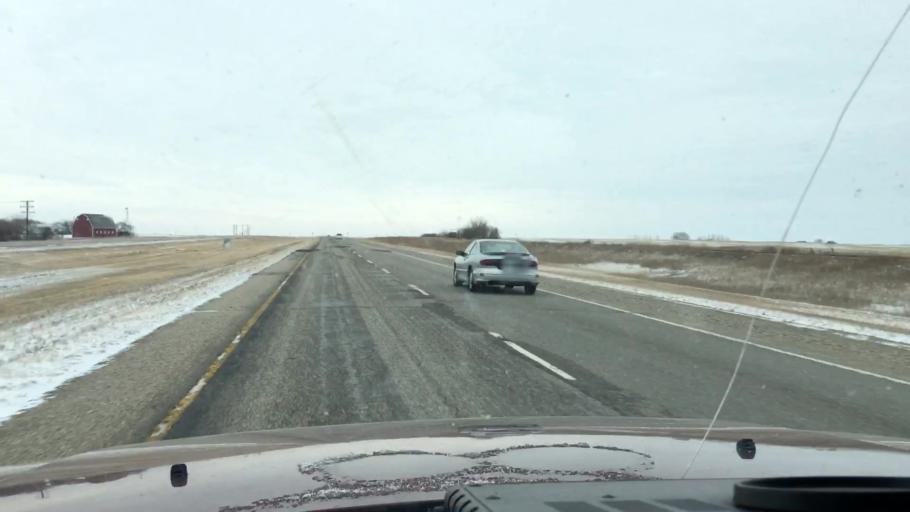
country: CA
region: Saskatchewan
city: Watrous
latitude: 51.4216
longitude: -106.1940
